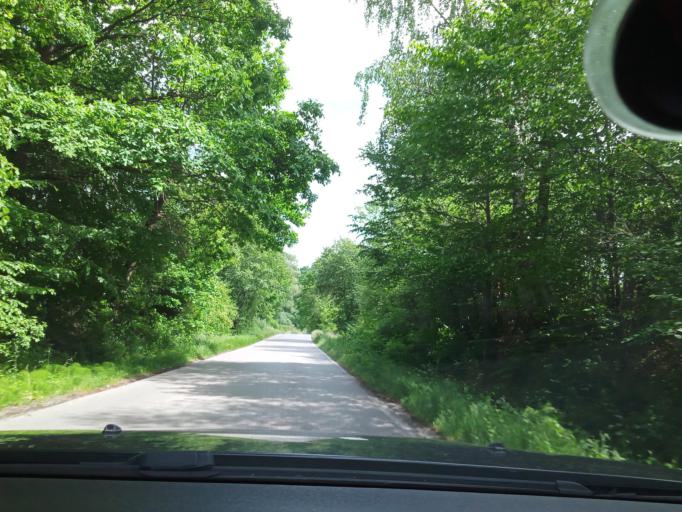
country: PL
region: Lesser Poland Voivodeship
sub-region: Powiat bochenski
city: Lapanow
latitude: 49.8532
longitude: 20.2548
